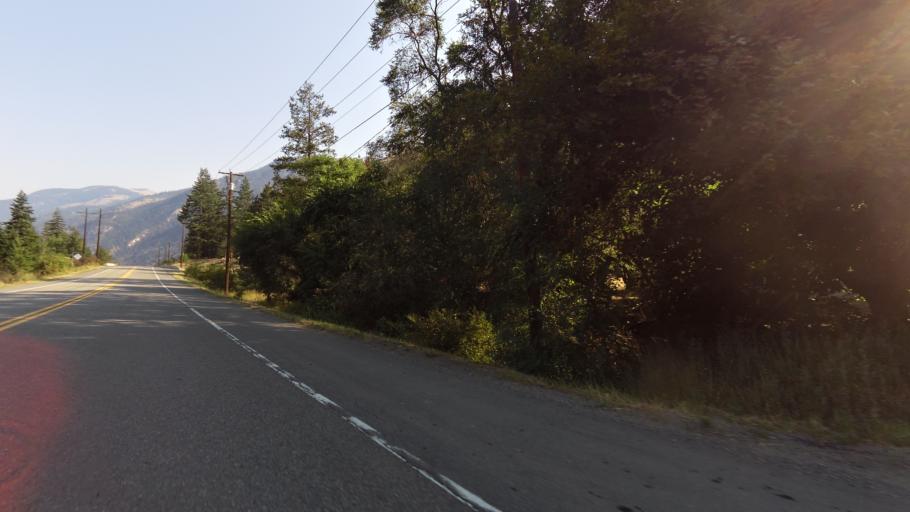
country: CA
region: British Columbia
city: Summerland
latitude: 49.2921
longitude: -120.0268
